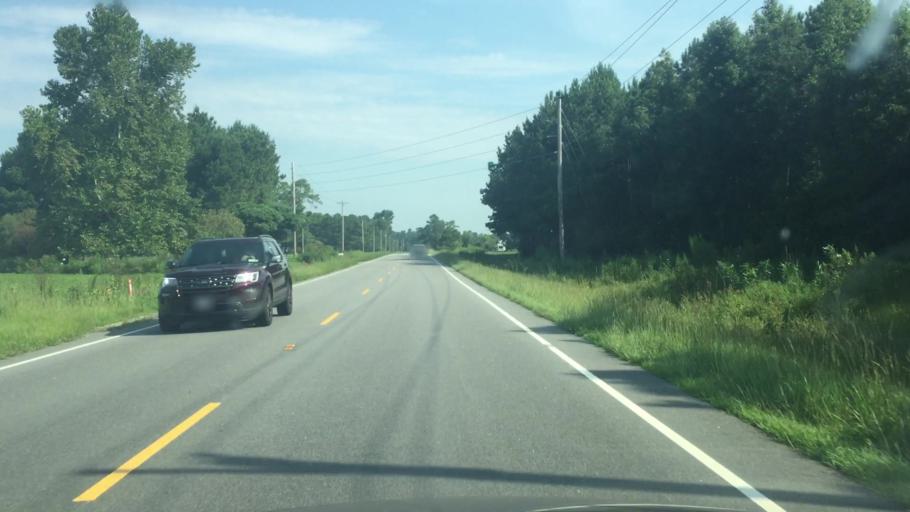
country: US
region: North Carolina
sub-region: Columbus County
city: Tabor City
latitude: 34.2243
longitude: -78.8242
